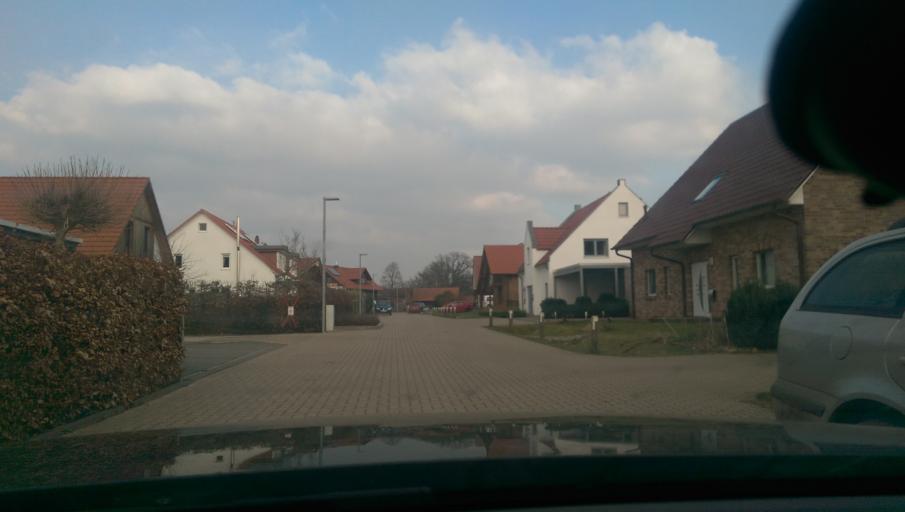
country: DE
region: Lower Saxony
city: Lindwedel
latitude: 52.5548
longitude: 9.6741
